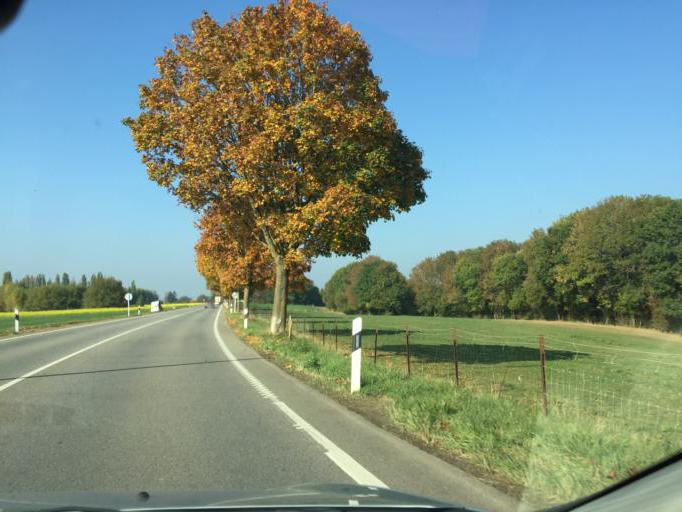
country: LU
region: Grevenmacher
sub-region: Canton de Remich
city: Dalheim
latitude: 49.5391
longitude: 6.2621
